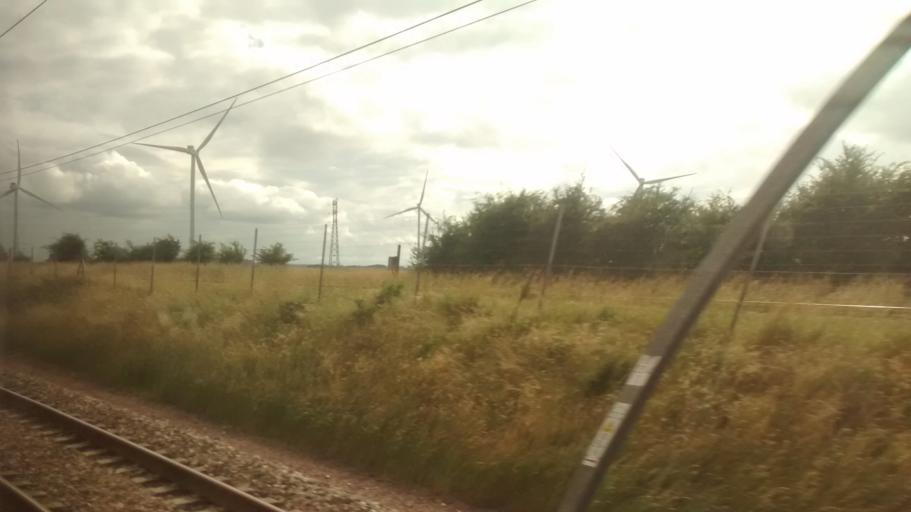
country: FR
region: Centre
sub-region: Departement d'Eure-et-Loir
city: Voves
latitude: 48.3220
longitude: 1.6686
